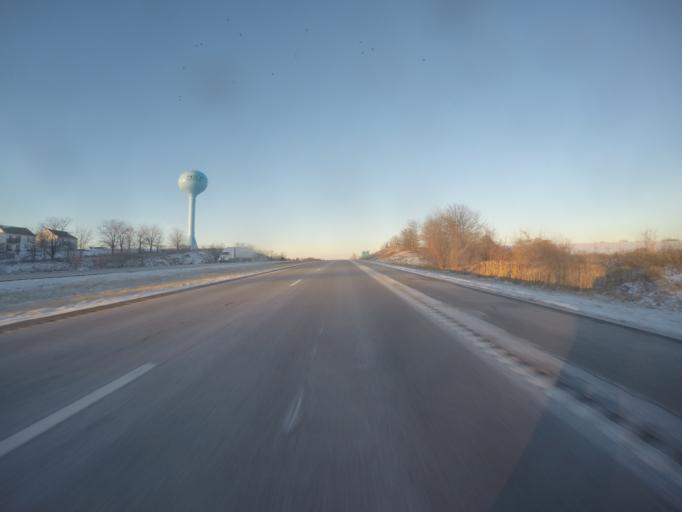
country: US
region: Missouri
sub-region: Platte County
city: Platte City
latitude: 39.3193
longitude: -94.7563
